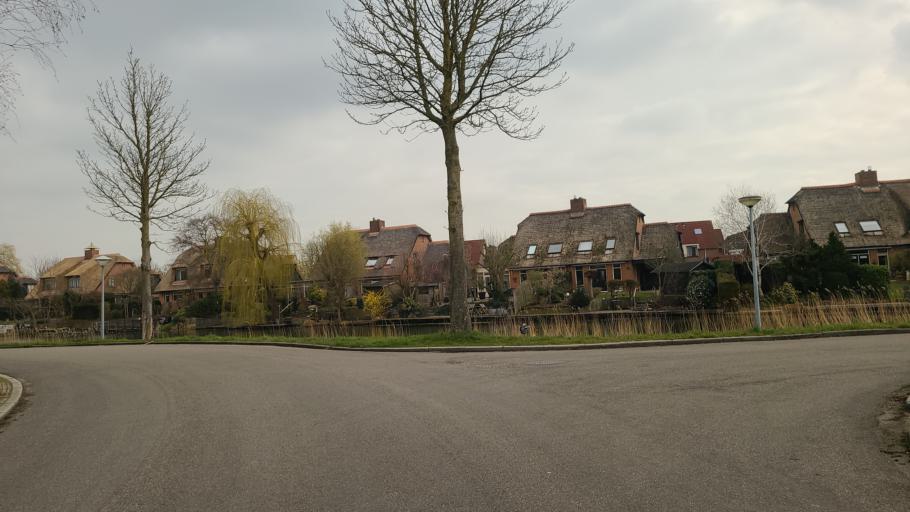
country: NL
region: Gelderland
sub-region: Gemeente Beuningen
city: Beuningen
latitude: 51.8526
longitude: 5.7556
